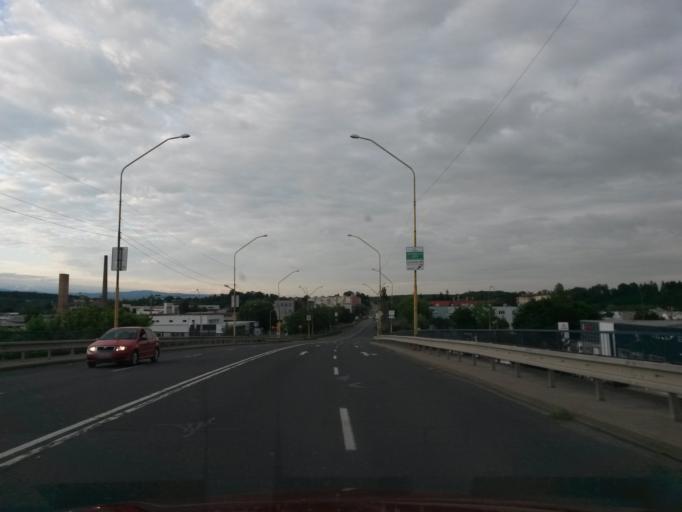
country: SK
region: Banskobystricky
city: Lucenec
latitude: 48.3332
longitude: 19.6731
